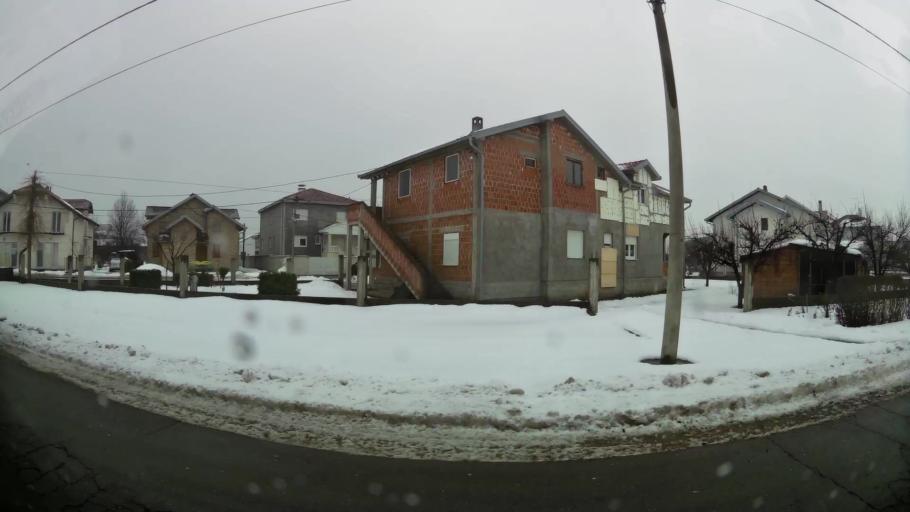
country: RS
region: Central Serbia
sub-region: Belgrade
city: Zemun
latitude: 44.8595
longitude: 20.3420
